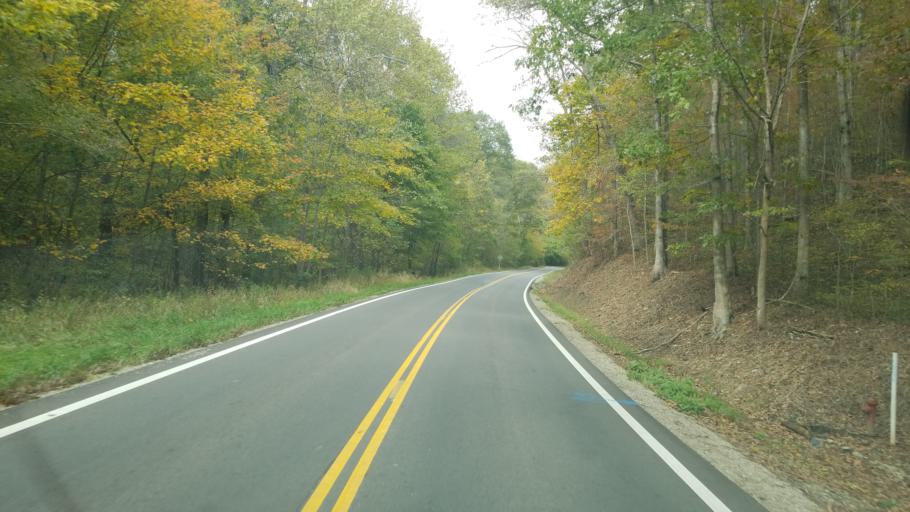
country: US
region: Ohio
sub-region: Jackson County
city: Wellston
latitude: 39.1565
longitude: -82.6161
